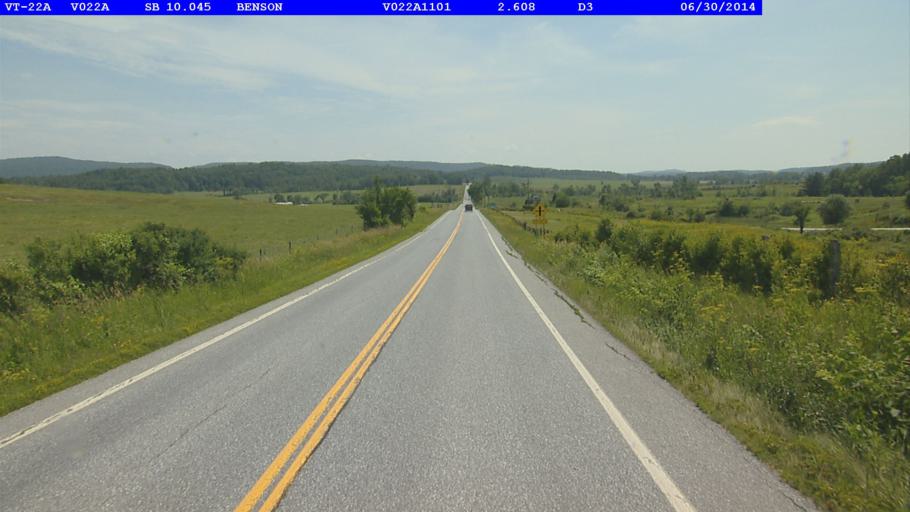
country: US
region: Vermont
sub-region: Rutland County
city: Fair Haven
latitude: 43.7060
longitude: -73.2965
